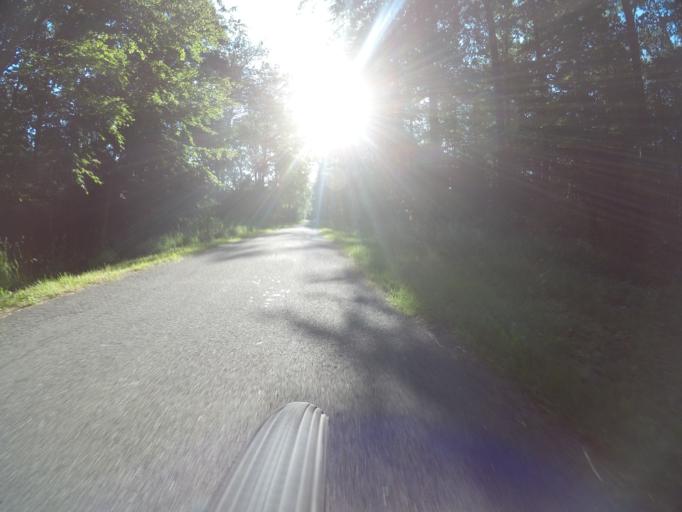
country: DE
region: Baden-Wuerttemberg
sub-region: Regierungsbezirk Stuttgart
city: Sindelfingen
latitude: 48.7207
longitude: 9.0366
